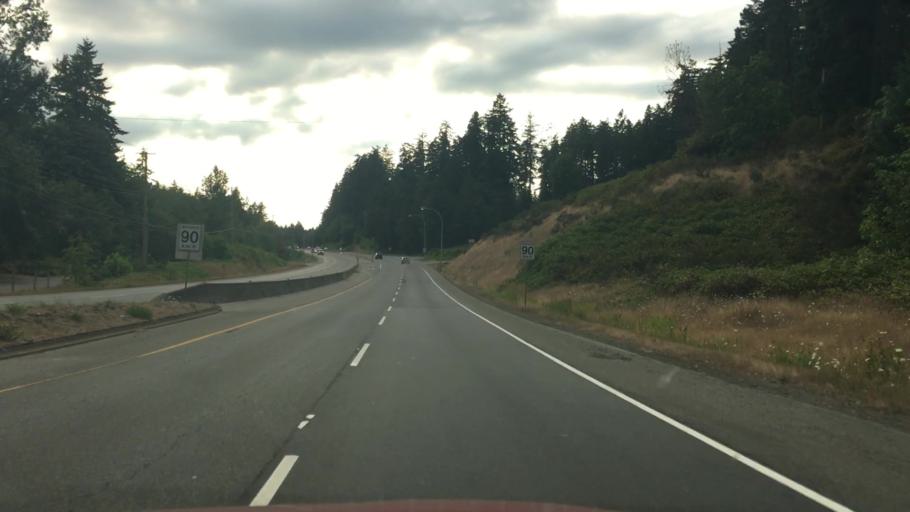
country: CA
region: British Columbia
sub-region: Regional District of Nanaimo
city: Parksville
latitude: 49.2642
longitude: -124.2060
